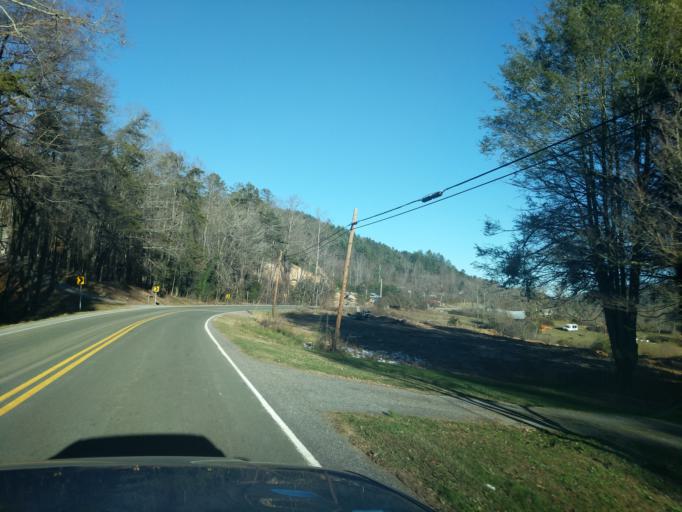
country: US
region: Georgia
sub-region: Rabun County
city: Clayton
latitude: 34.8758
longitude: -83.4483
